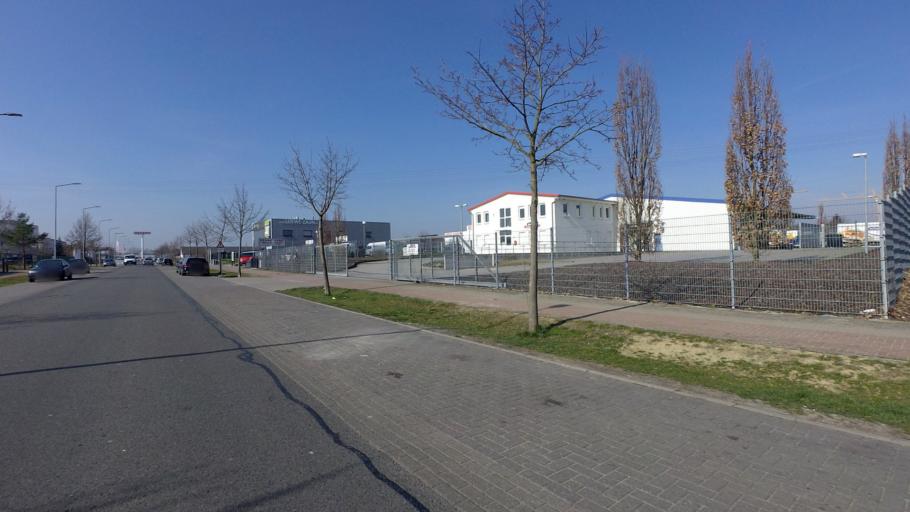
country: DE
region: Berlin
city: Lichtenrade
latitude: 52.3599
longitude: 13.4389
